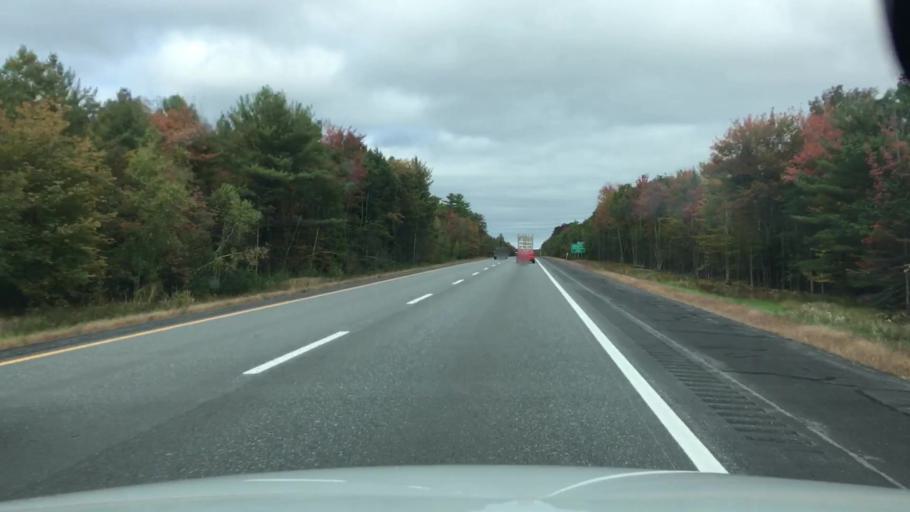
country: US
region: Maine
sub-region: Somerset County
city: Palmyra
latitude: 44.8230
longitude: -69.3275
